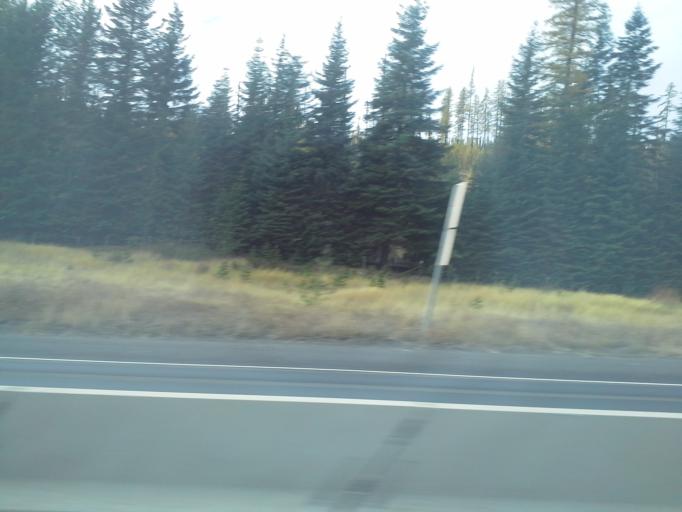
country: US
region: Oregon
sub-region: Union County
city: La Grande
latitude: 45.4256
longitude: -118.3542
